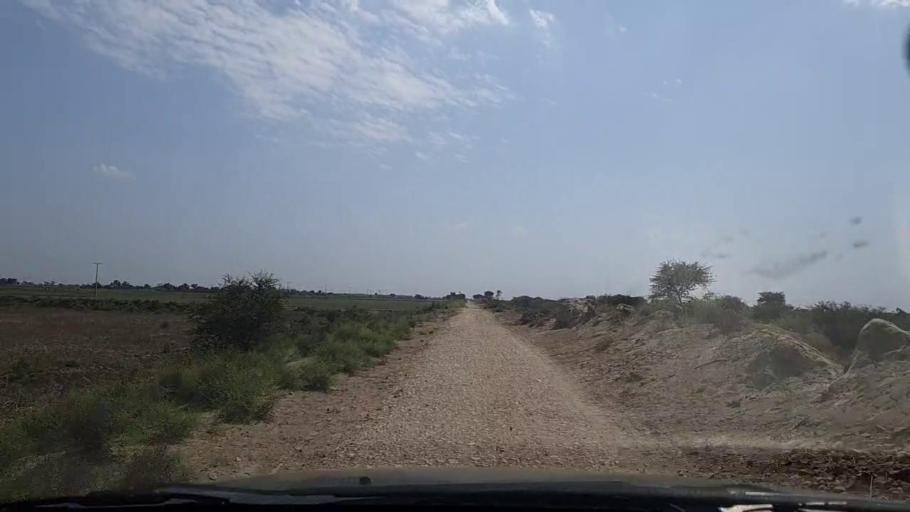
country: PK
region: Sindh
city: Mirpur Batoro
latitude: 24.5874
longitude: 68.1971
